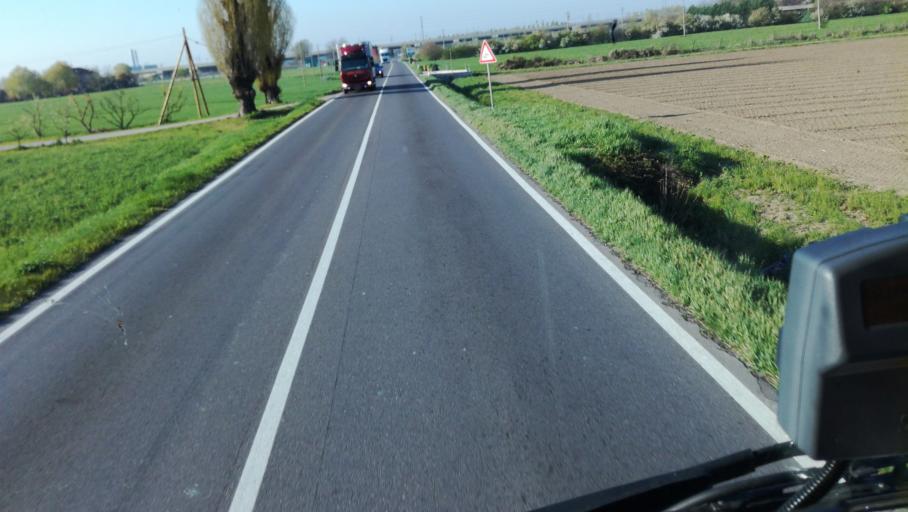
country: IT
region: Emilia-Romagna
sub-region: Provincia di Modena
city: Albareto
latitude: 44.6967
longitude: 10.9471
